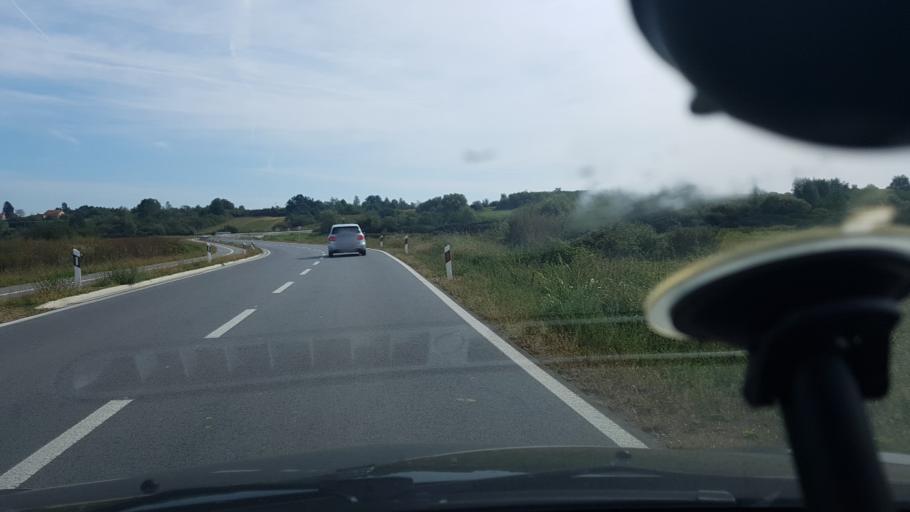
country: HR
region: Krapinsko-Zagorska
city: Marija Bistrica
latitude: 46.0581
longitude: 16.1565
